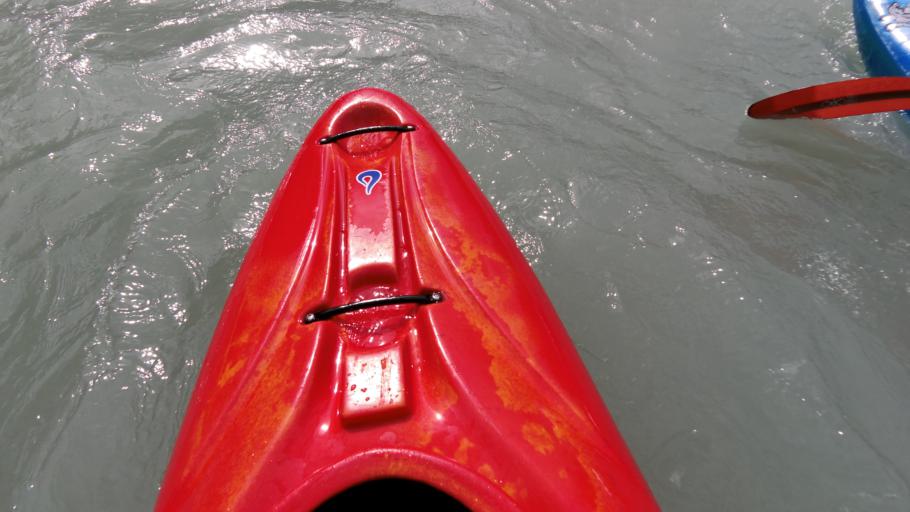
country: AT
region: Tyrol
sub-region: Politischer Bezirk Landeck
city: Landeck
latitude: 47.1242
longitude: 10.5834
